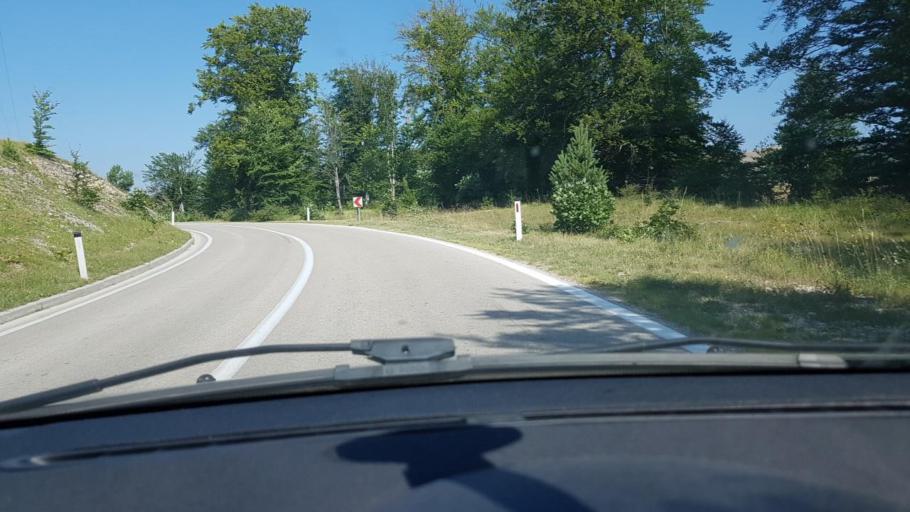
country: BA
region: Federation of Bosnia and Herzegovina
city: Bosansko Grahovo
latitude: 44.1098
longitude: 16.5475
